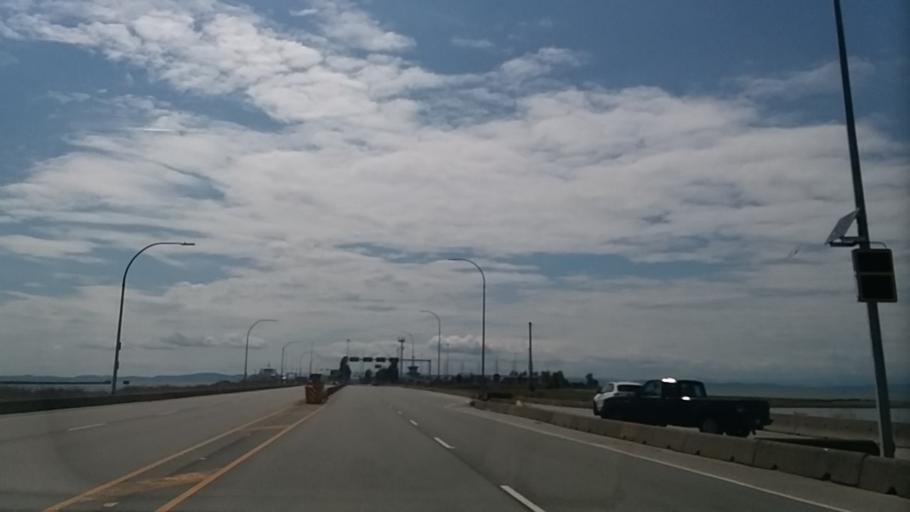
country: US
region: Washington
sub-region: Whatcom County
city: Point Roberts
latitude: 49.0141
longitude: -123.1192
